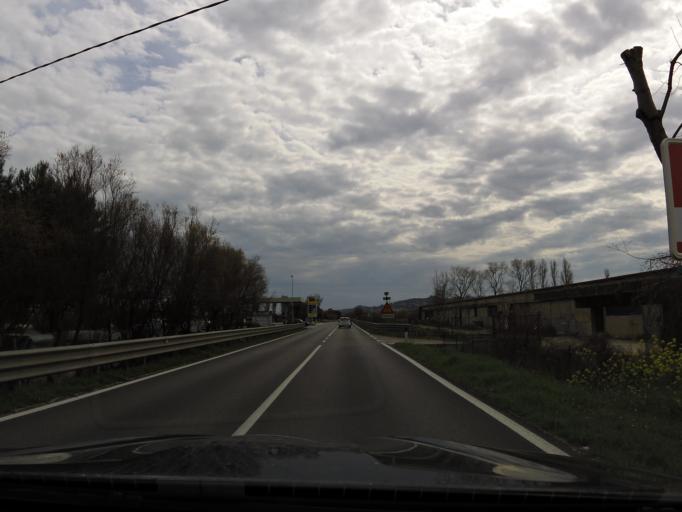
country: IT
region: The Marches
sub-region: Provincia di Macerata
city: Porto Recanati
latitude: 43.4027
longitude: 13.6779
